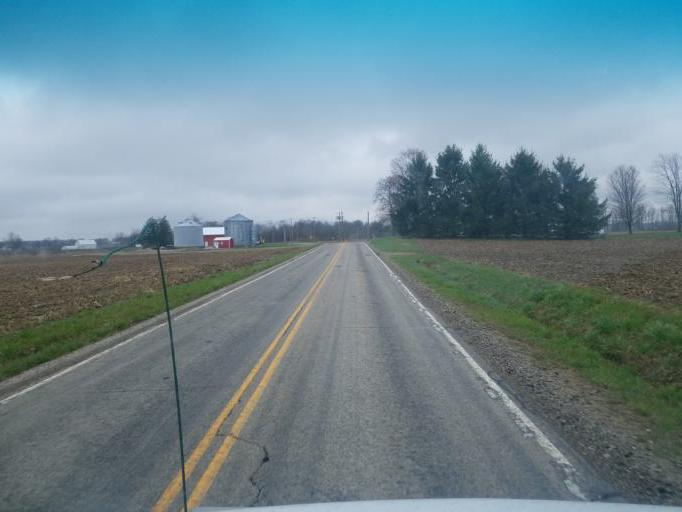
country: US
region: Ohio
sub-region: Richland County
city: Shelby
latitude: 40.9201
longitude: -82.6413
